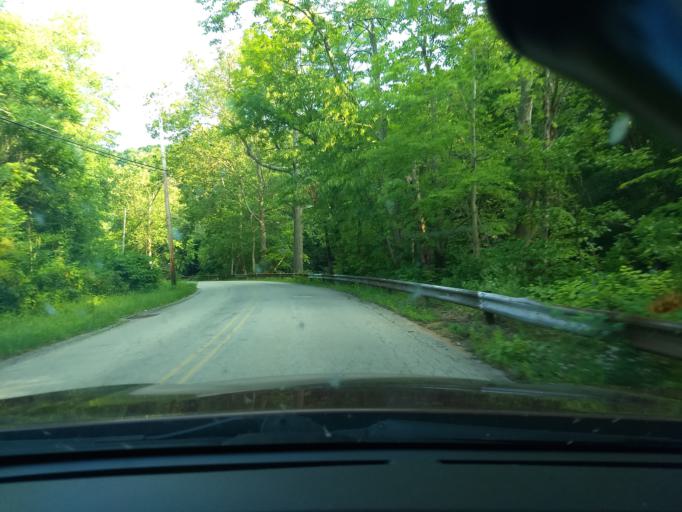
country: US
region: Pennsylvania
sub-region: Westmoreland County
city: Trafford
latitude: 40.3732
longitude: -79.7641
